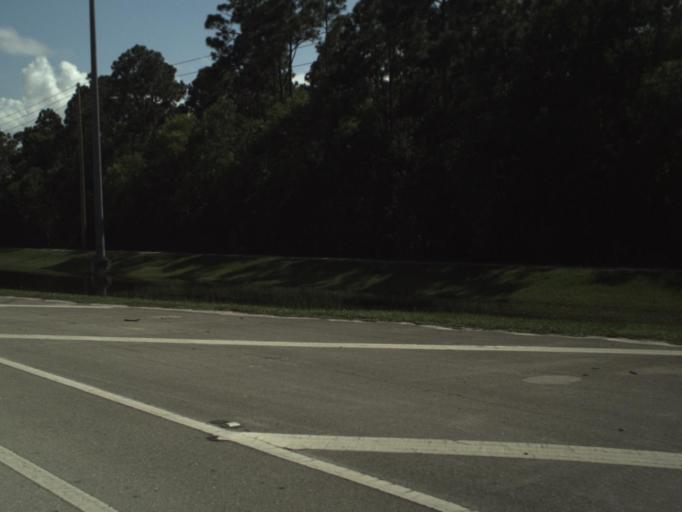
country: US
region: Florida
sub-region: Palm Beach County
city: Wellington
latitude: 26.5743
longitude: -80.2060
